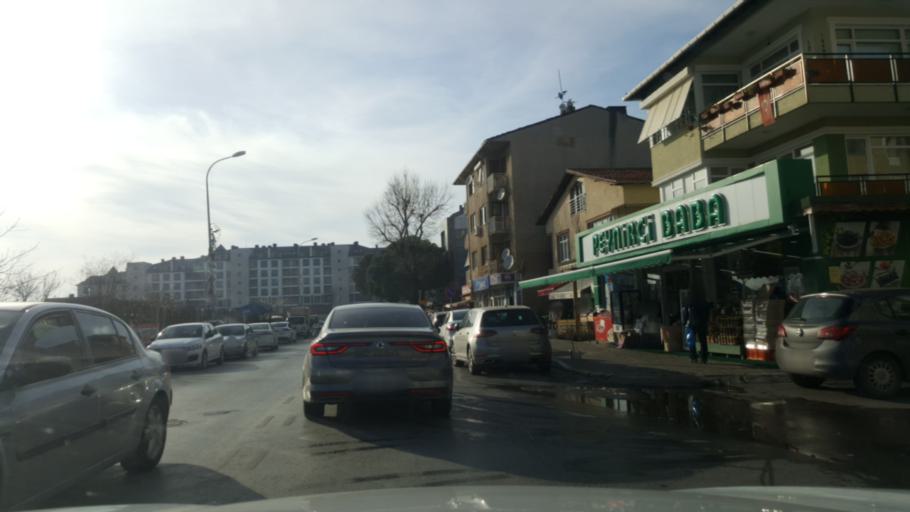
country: TR
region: Istanbul
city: Icmeler
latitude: 40.8177
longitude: 29.3029
